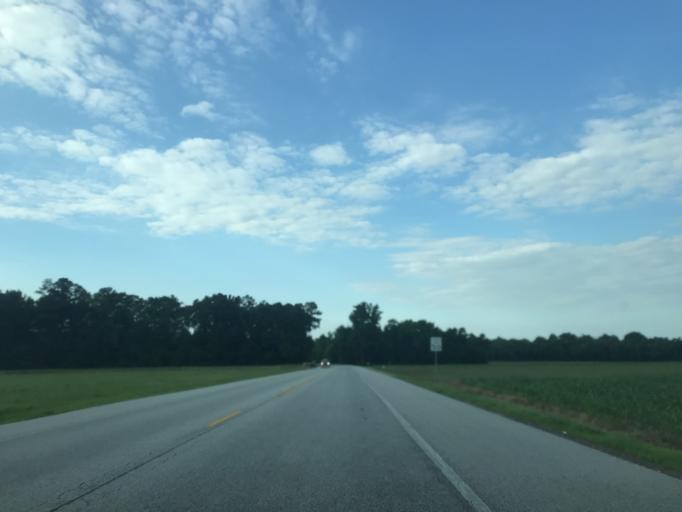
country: US
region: Maryland
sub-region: Caroline County
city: Federalsburg
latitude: 38.7507
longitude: -75.7921
